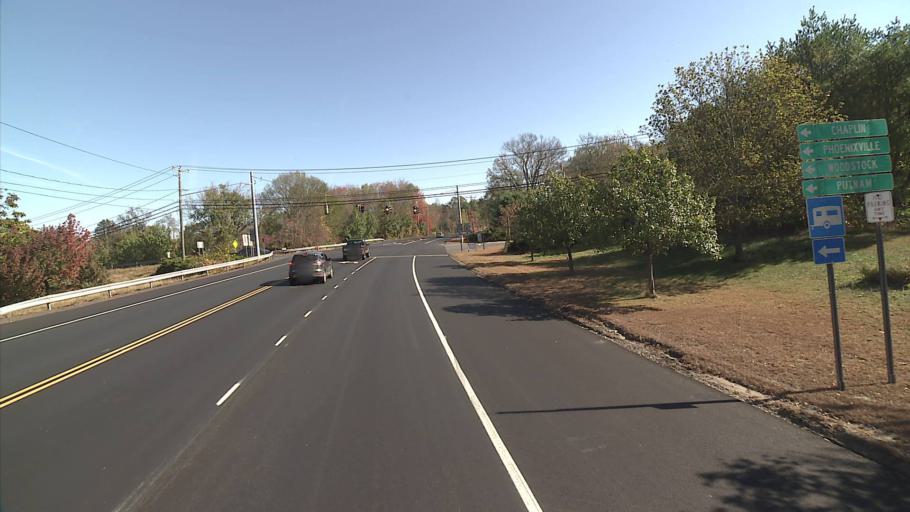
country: US
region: Connecticut
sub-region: Windham County
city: Windham
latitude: 41.7707
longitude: -72.1350
